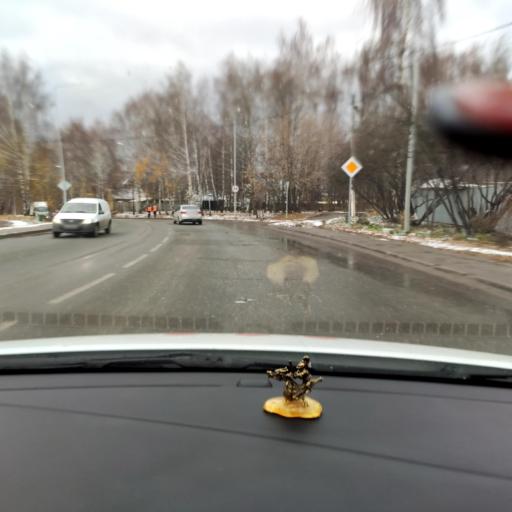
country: RU
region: Tatarstan
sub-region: Zelenodol'skiy Rayon
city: Zelenodolsk
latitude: 55.8470
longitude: 48.5489
